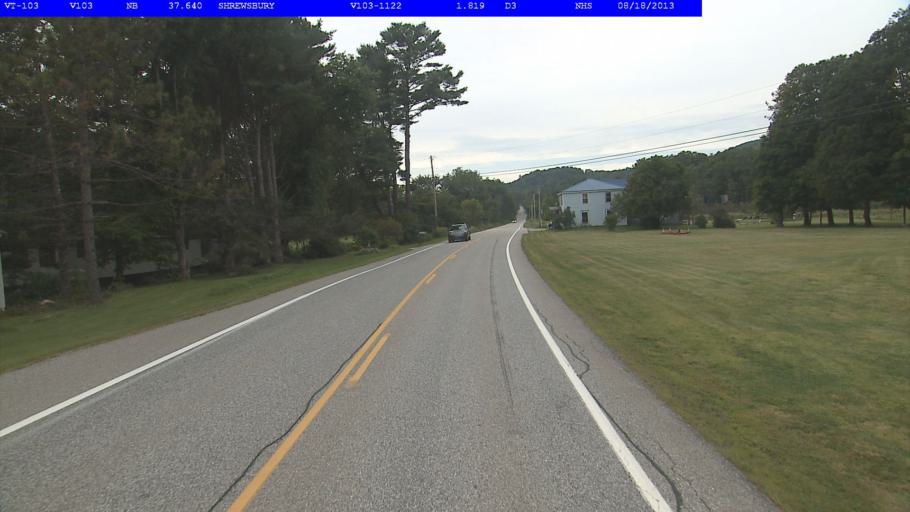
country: US
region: Vermont
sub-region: Rutland County
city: Rutland
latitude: 43.4998
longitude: -72.8973
